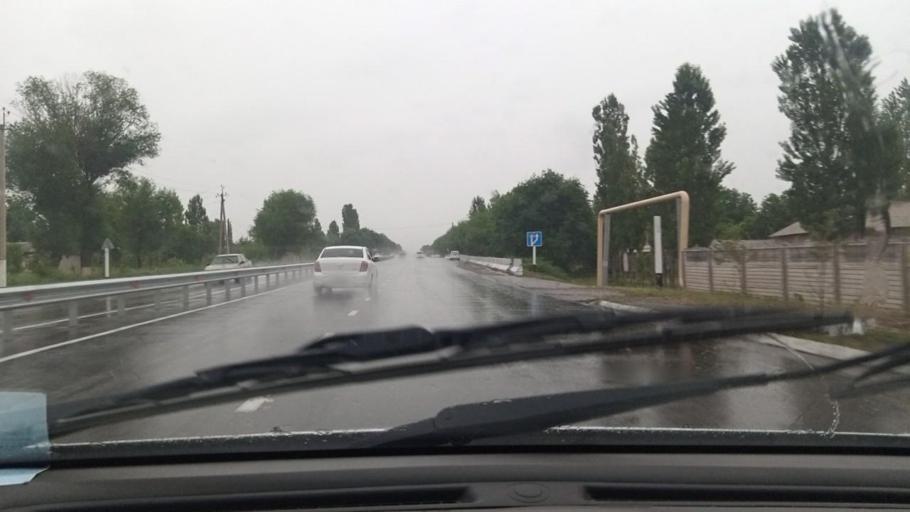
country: UZ
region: Toshkent
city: Angren
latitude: 40.9791
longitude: 70.0125
